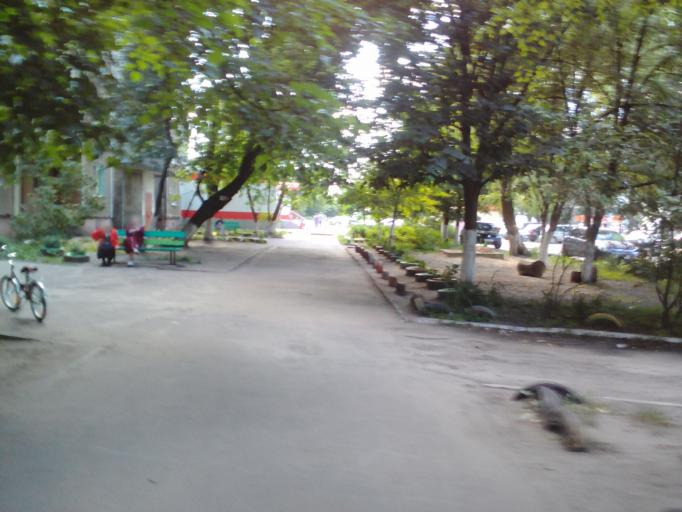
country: RU
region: Kursk
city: Voroshnevo
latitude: 51.6674
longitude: 36.0933
